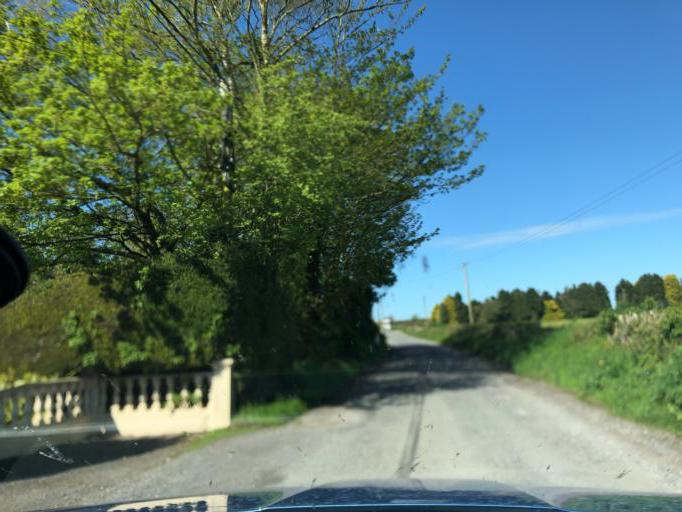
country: IE
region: Connaught
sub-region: County Galway
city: Portumna
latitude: 53.1789
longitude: -8.1849
